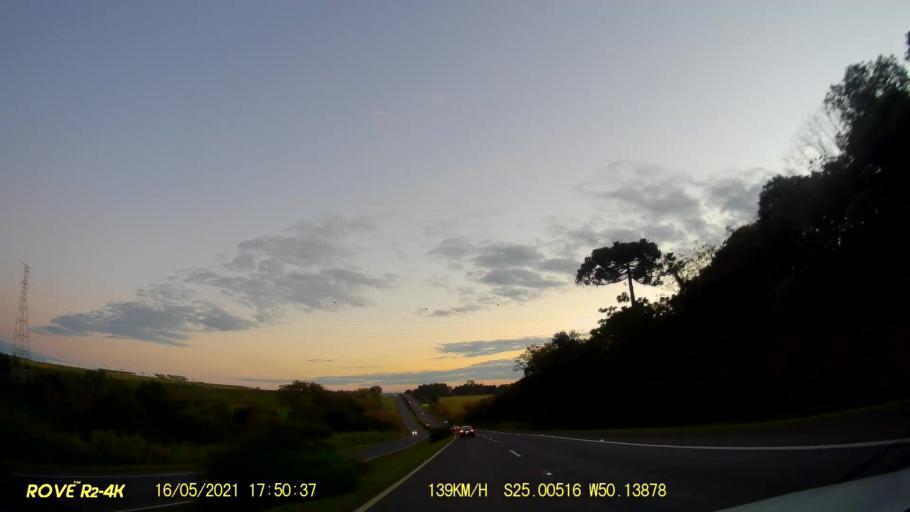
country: BR
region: Parana
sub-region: Carambei
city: Carambei
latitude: -25.0053
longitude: -50.1384
